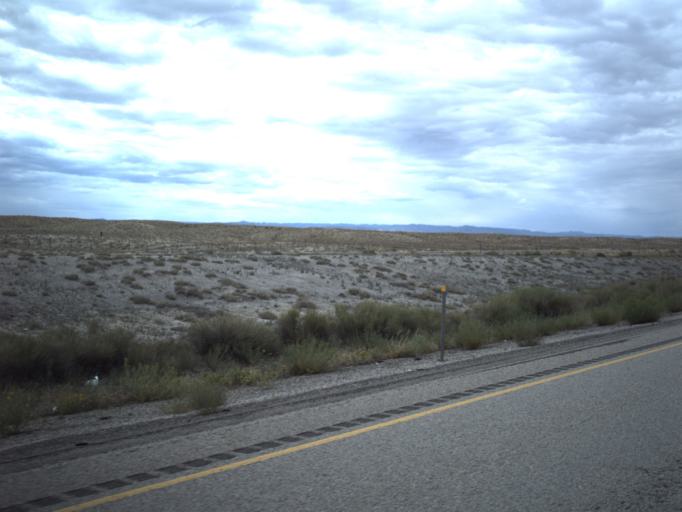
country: US
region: Utah
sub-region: Grand County
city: Moab
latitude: 39.0027
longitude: -109.3164
